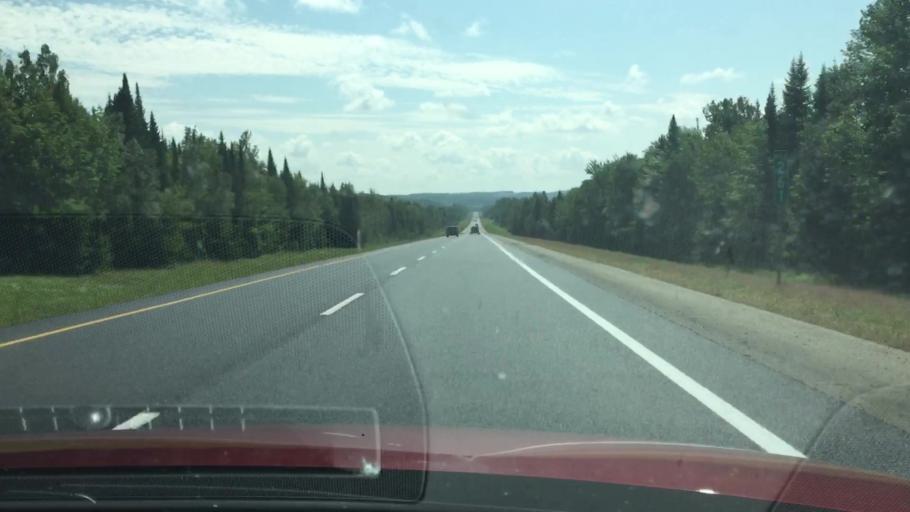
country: US
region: Maine
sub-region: Penobscot County
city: Patten
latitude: 45.8298
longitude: -68.4329
